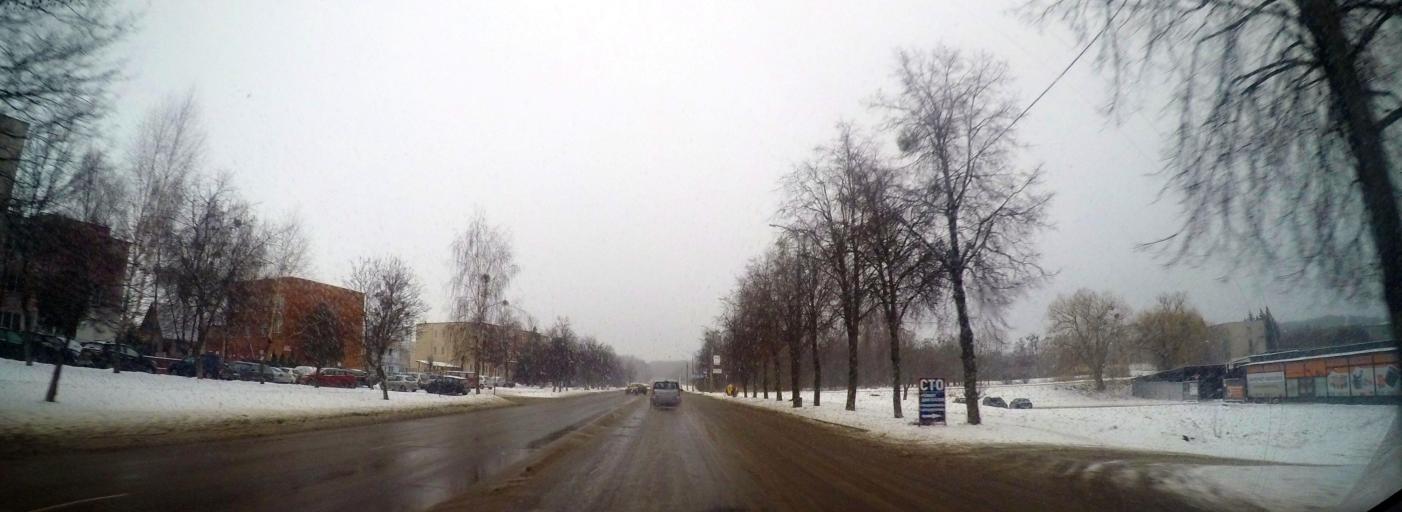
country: BY
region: Grodnenskaya
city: Hrodna
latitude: 53.6866
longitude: 23.8792
